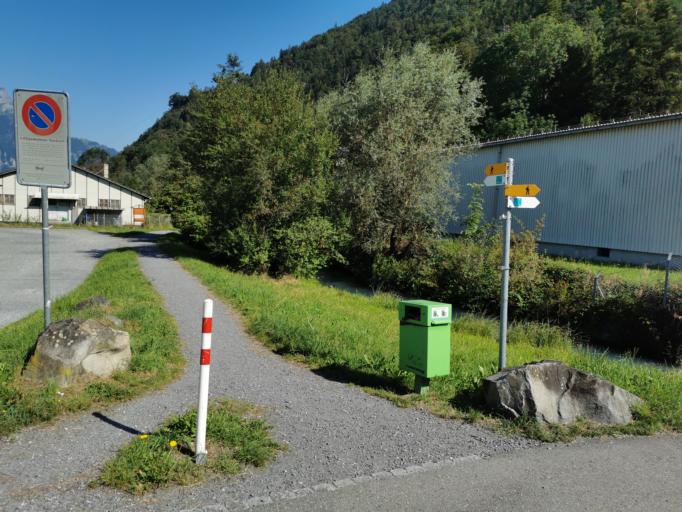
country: CH
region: Uri
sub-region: Uri
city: Altdorf
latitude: 46.8881
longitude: 8.6340
